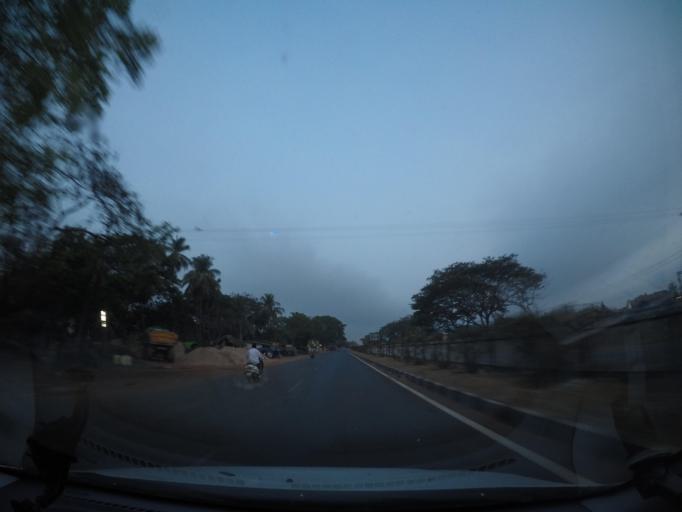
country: IN
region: Andhra Pradesh
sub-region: West Godavari
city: Tadepallegudem
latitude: 16.8193
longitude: 81.3990
